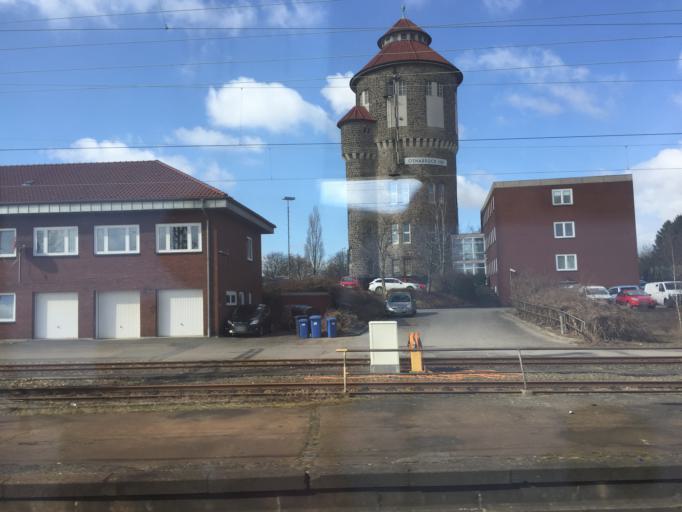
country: DE
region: Lower Saxony
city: Osnabrueck
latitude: 52.2743
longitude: 8.0625
